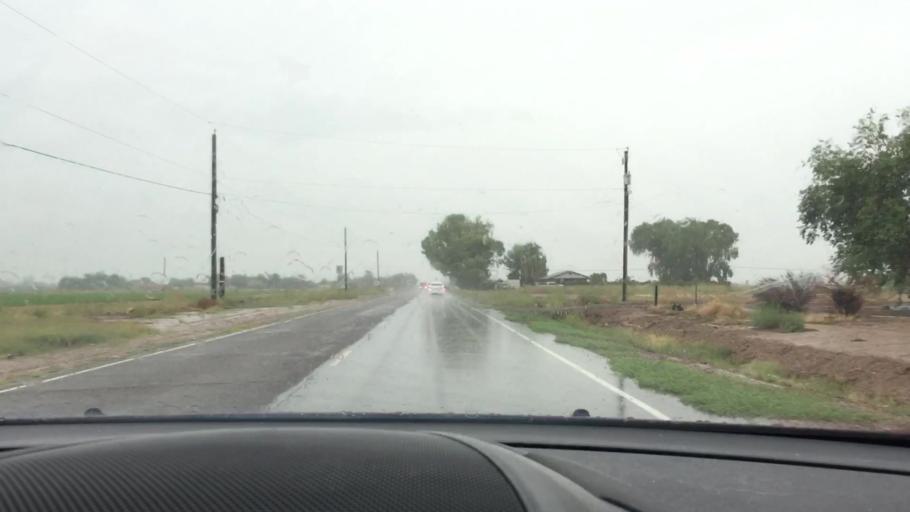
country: US
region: Arizona
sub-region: Maricopa County
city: Scottsdale
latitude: 33.4709
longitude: -111.8827
